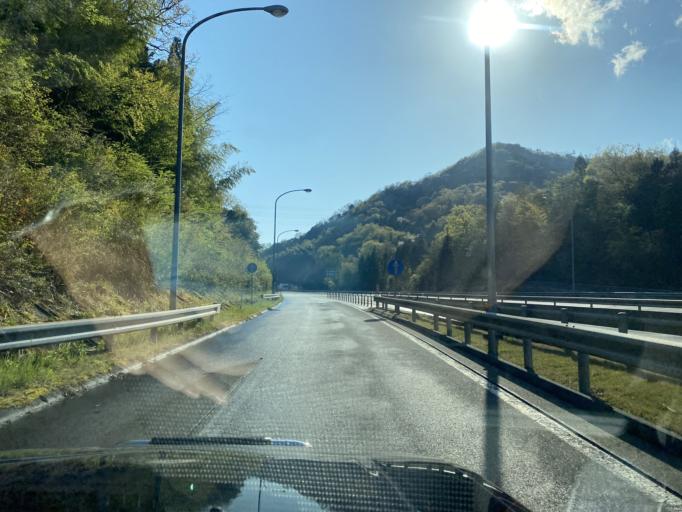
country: JP
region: Kyoto
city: Ayabe
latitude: 35.3266
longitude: 135.2555
